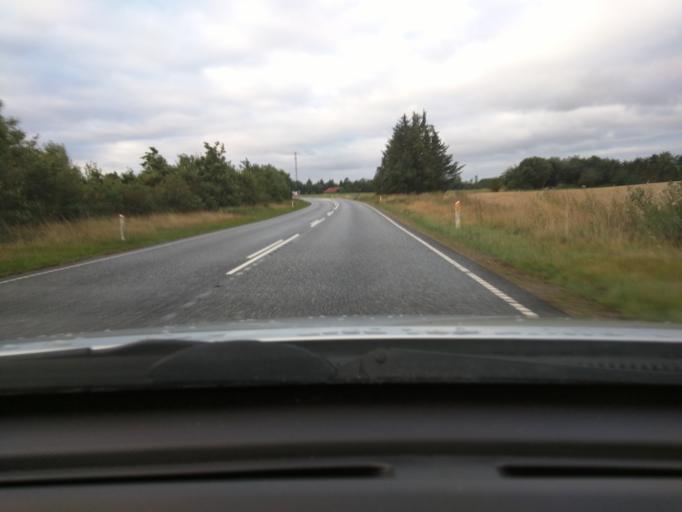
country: DK
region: Central Jutland
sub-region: Silkeborg Kommune
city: Kjellerup
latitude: 56.2708
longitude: 9.3157
